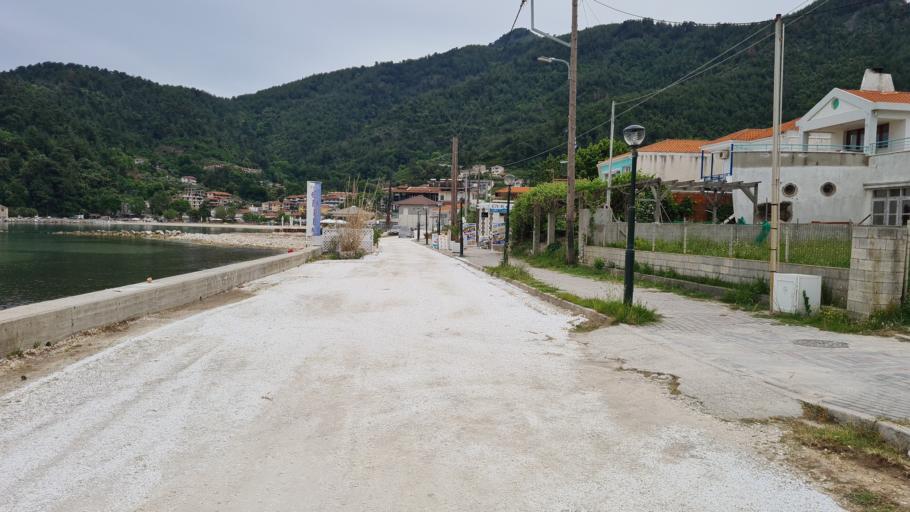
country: GR
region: East Macedonia and Thrace
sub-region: Nomos Kavalas
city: Potamia
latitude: 40.7122
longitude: 24.7585
